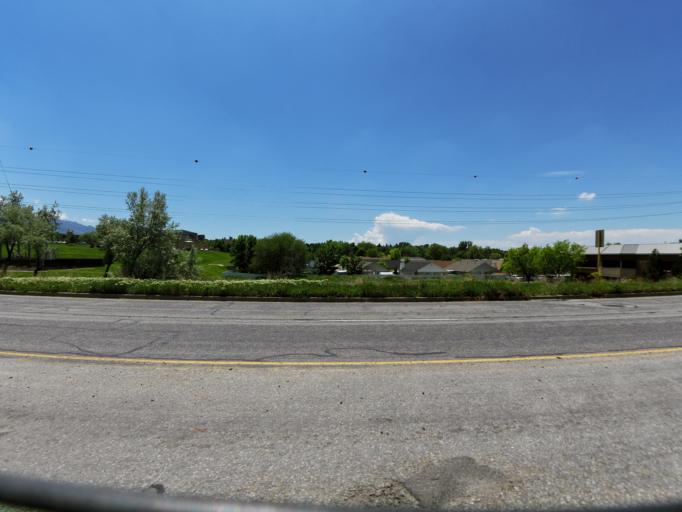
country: US
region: Utah
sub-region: Weber County
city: South Ogden
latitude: 41.1886
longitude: -111.9559
